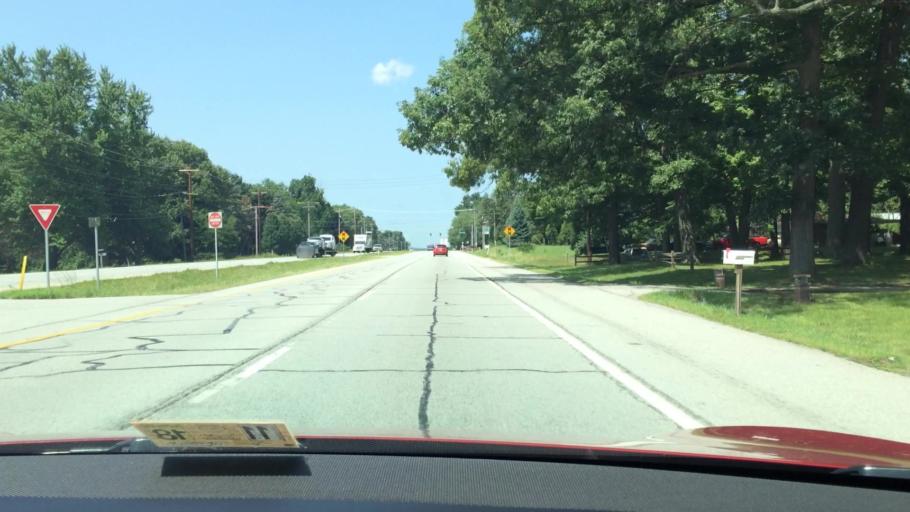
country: US
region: Indiana
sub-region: Saint Joseph County
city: South Bend
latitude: 41.6720
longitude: -86.3766
